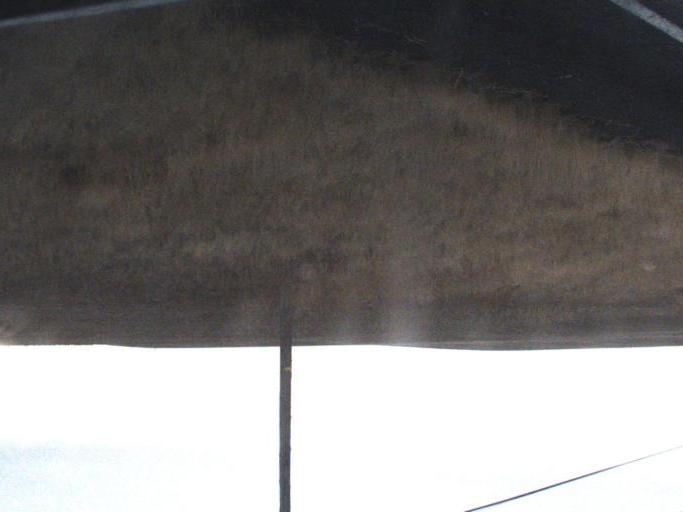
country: US
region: Washington
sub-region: Lincoln County
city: Davenport
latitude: 47.6960
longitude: -118.1410
